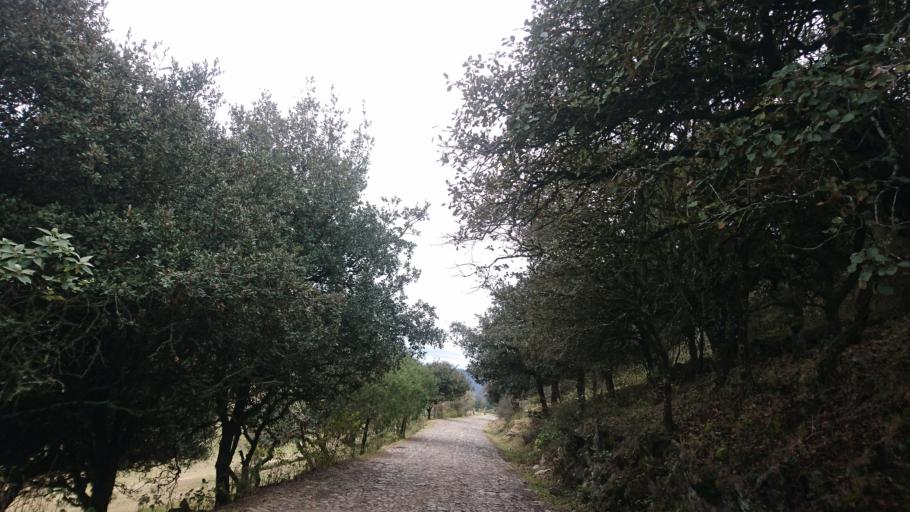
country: MX
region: San Luis Potosi
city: Zaragoza
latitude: 22.0737
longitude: -100.6387
